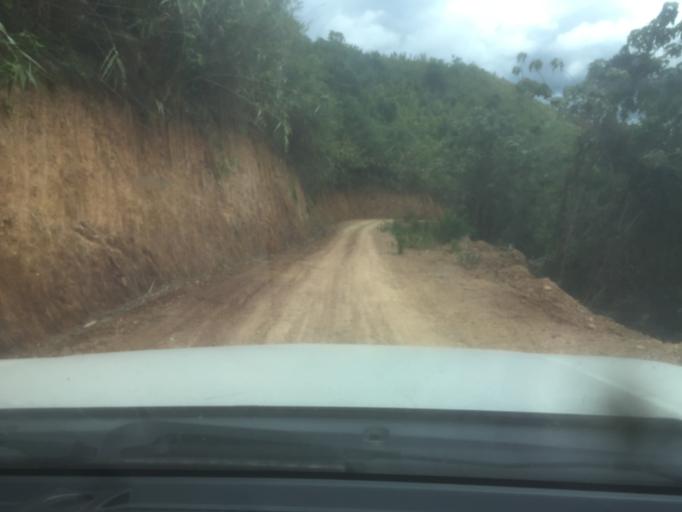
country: LA
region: Phongsali
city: Khoa
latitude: 20.9273
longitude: 102.5321
